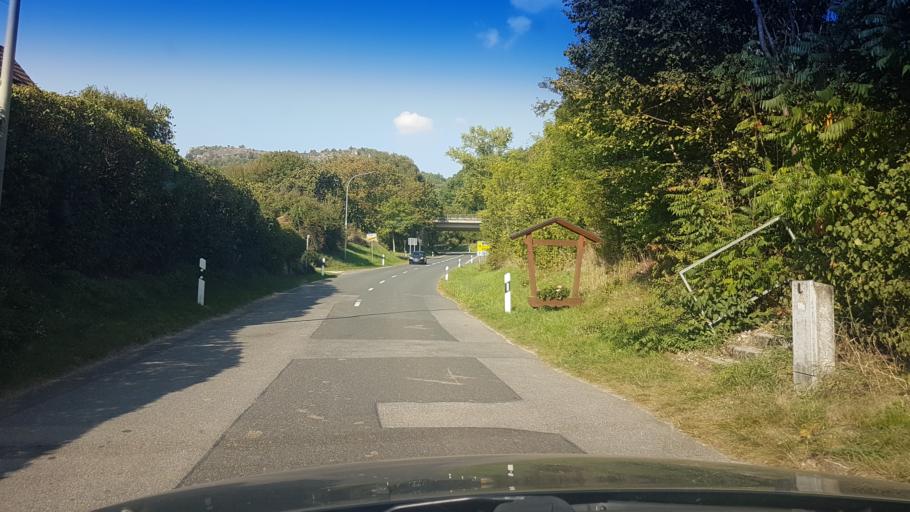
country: DE
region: Bavaria
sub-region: Upper Franconia
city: Bad Staffelstein
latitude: 50.0801
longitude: 11.0264
